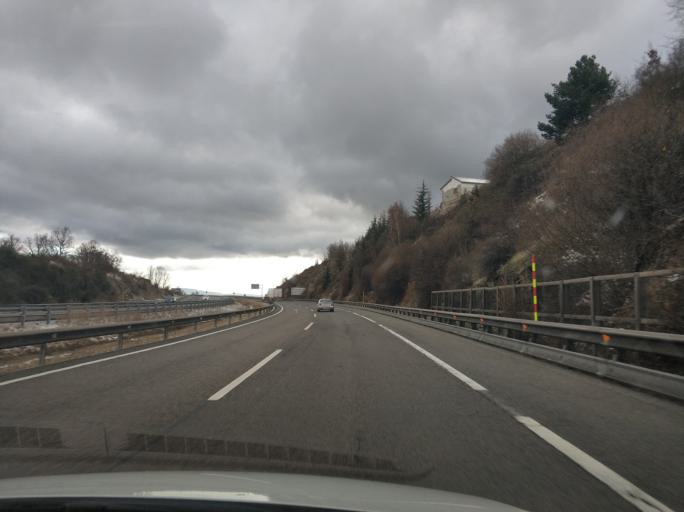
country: ES
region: Madrid
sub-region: Provincia de Madrid
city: Robregordo
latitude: 41.1031
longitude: -3.5929
